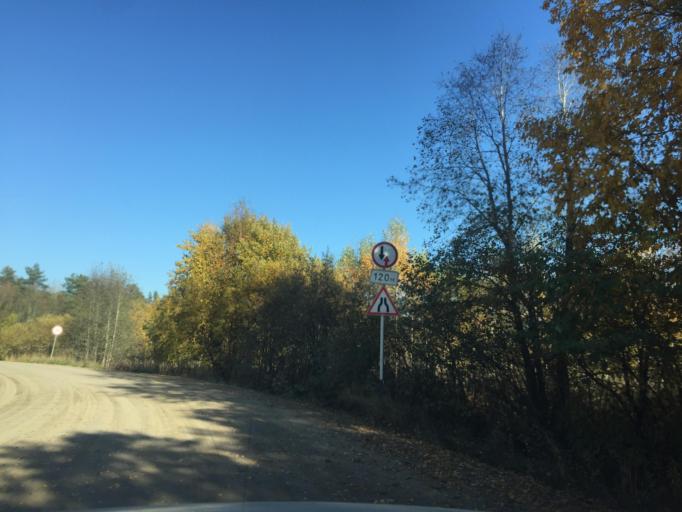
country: RU
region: Leningrad
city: Kuznechnoye
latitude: 61.3221
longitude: 29.9472
